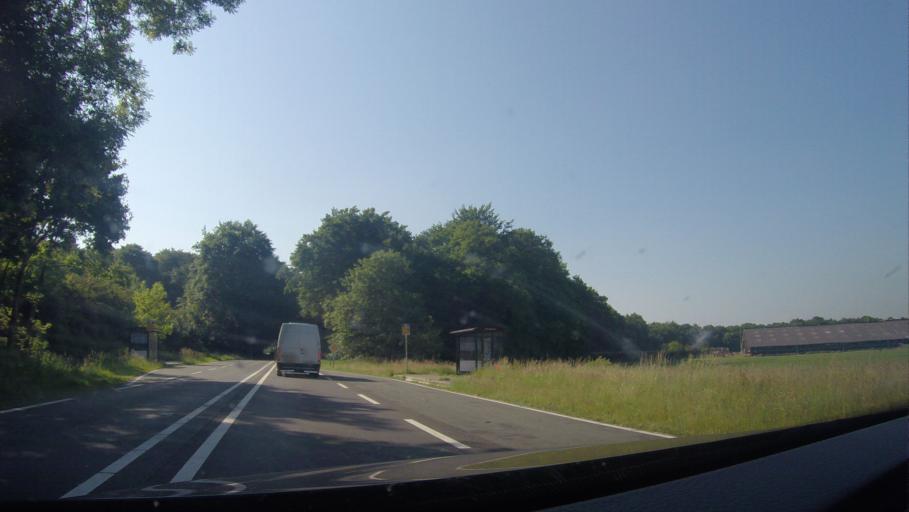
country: NL
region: Overijssel
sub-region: Gemeente Raalte
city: Heino
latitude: 52.4531
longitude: 6.2188
